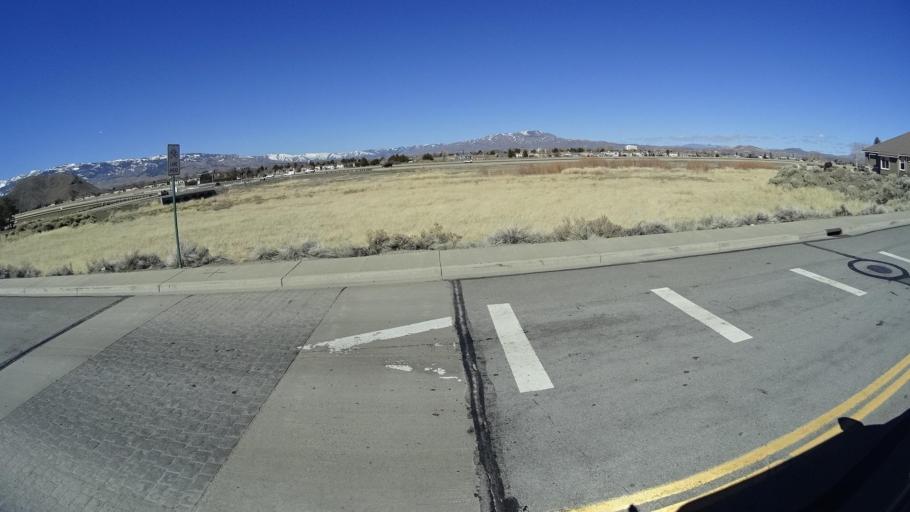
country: US
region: Nevada
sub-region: Washoe County
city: Sparks
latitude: 39.4848
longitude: -119.7340
